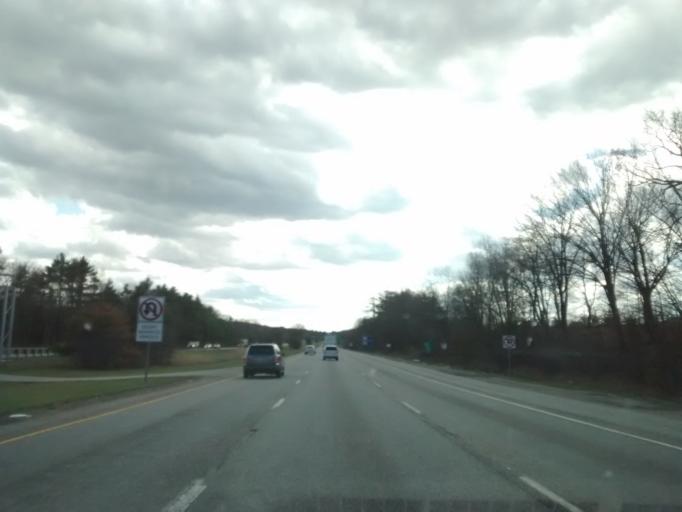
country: US
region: Massachusetts
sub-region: Worcester County
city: Berlin
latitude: 42.3553
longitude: -71.6095
